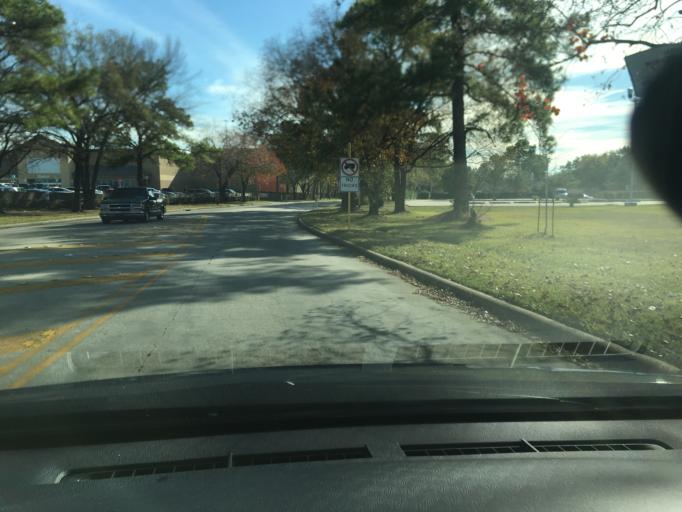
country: US
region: Texas
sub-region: Harris County
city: Cloverleaf
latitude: 29.8075
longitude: -95.1664
